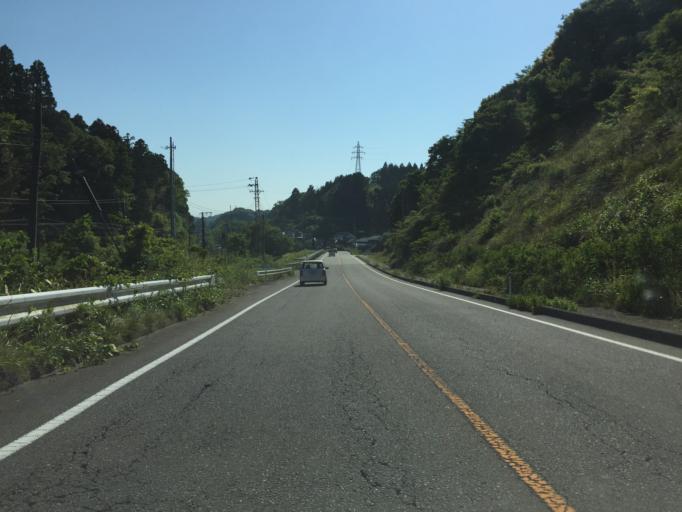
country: JP
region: Fukushima
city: Iwaki
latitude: 36.9442
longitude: 140.8225
